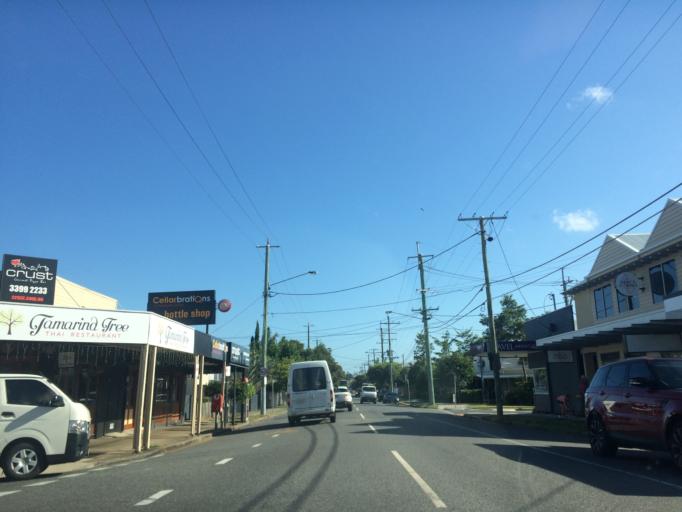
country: AU
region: Queensland
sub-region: Brisbane
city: Balmoral
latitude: -27.4622
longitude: 153.0603
